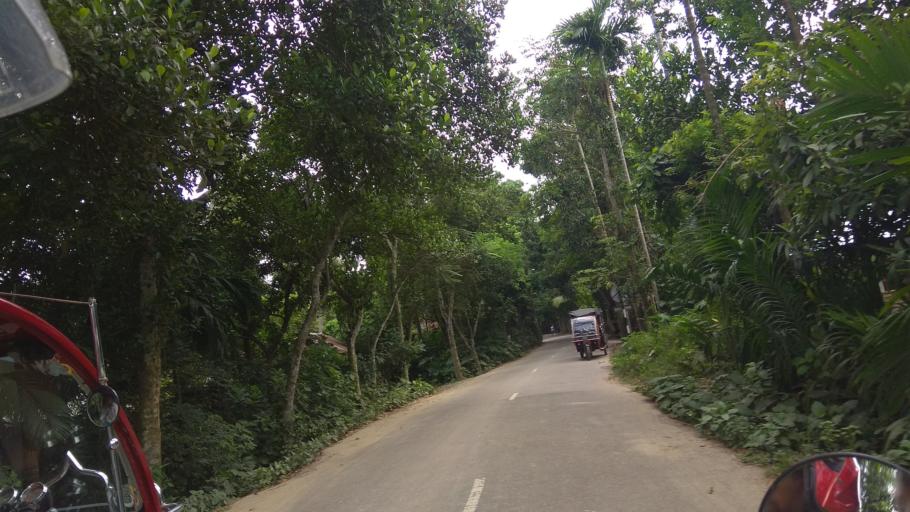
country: BD
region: Khulna
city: Kalia
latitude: 23.1645
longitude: 89.6450
